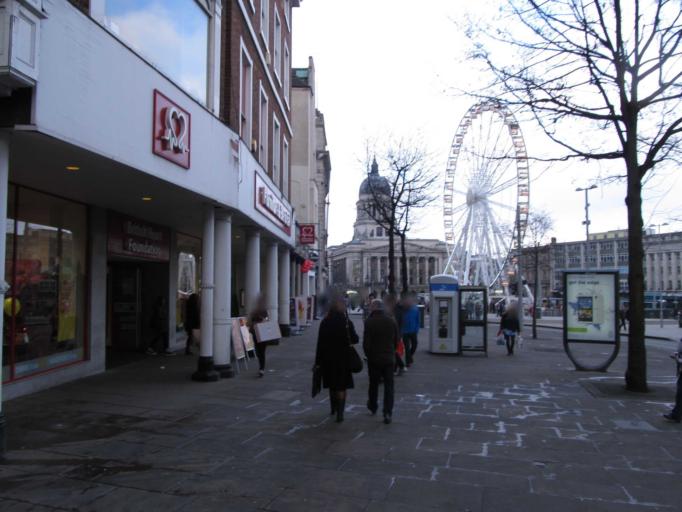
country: GB
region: England
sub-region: Nottingham
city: Nottingham
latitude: 52.9537
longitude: -1.1521
